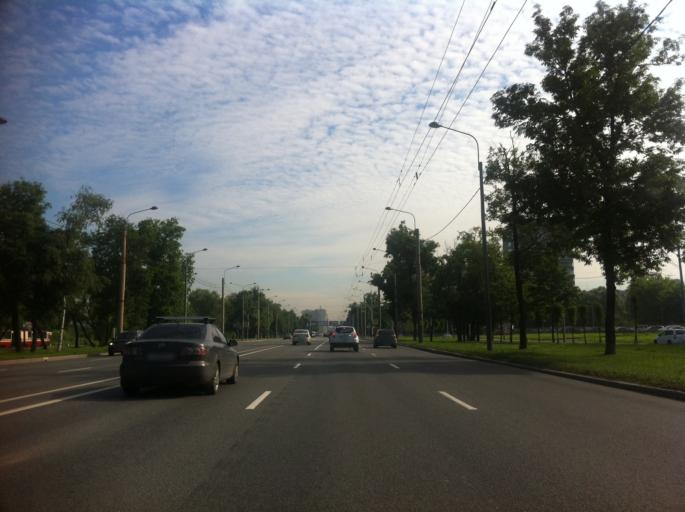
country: RU
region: St.-Petersburg
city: Uritsk
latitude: 59.8379
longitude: 30.2014
